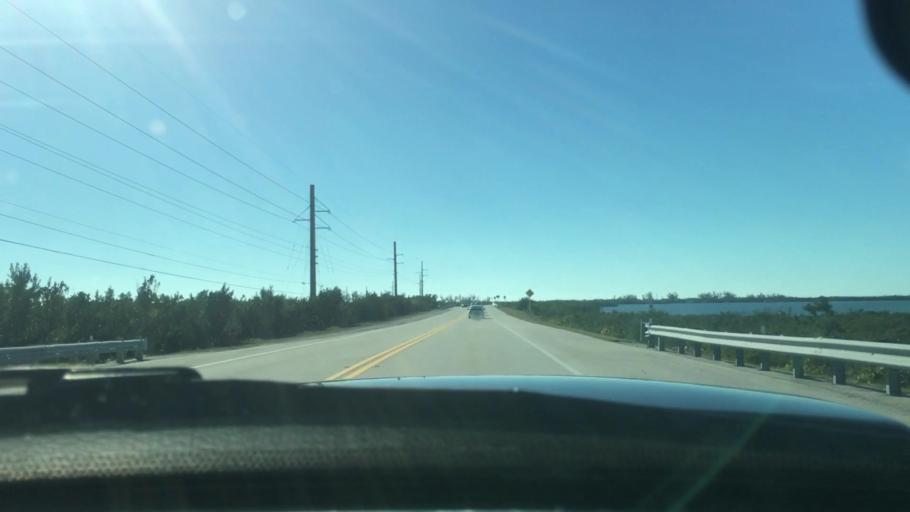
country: US
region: Florida
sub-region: Monroe County
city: Cudjoe Key
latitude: 24.6501
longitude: -81.5565
